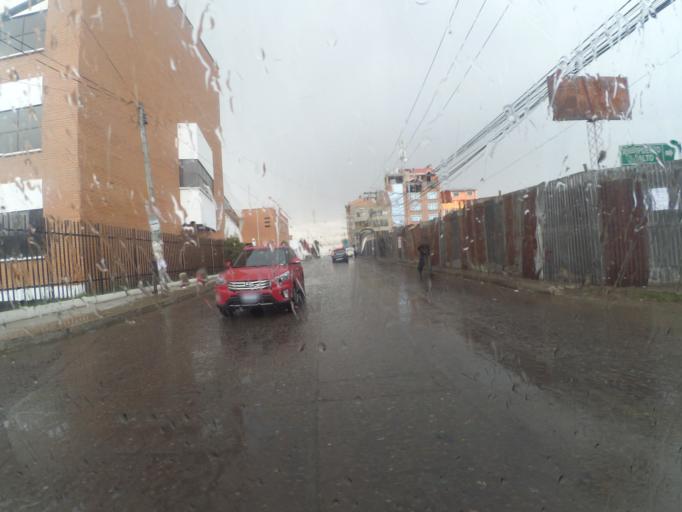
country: BO
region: La Paz
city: La Paz
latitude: -16.5174
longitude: -68.1658
